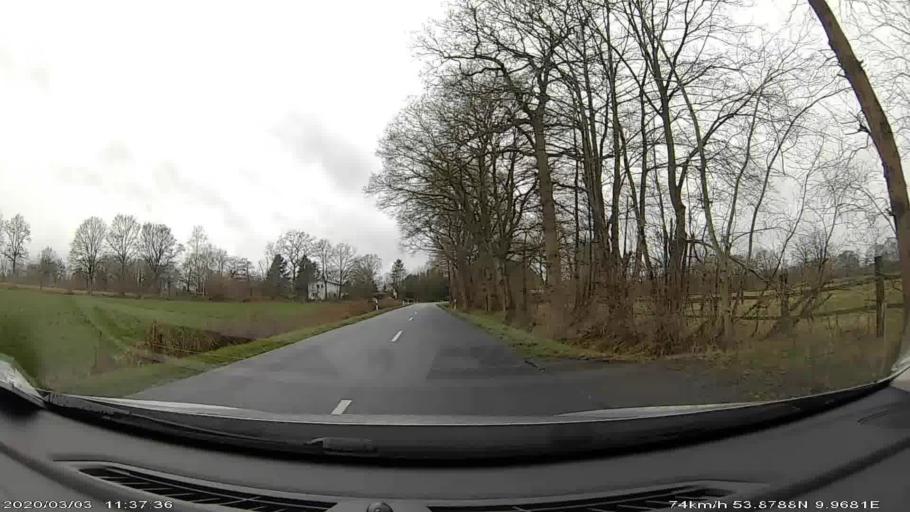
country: DE
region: Schleswig-Holstein
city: Schmalfeld
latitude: 53.8791
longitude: 9.9639
